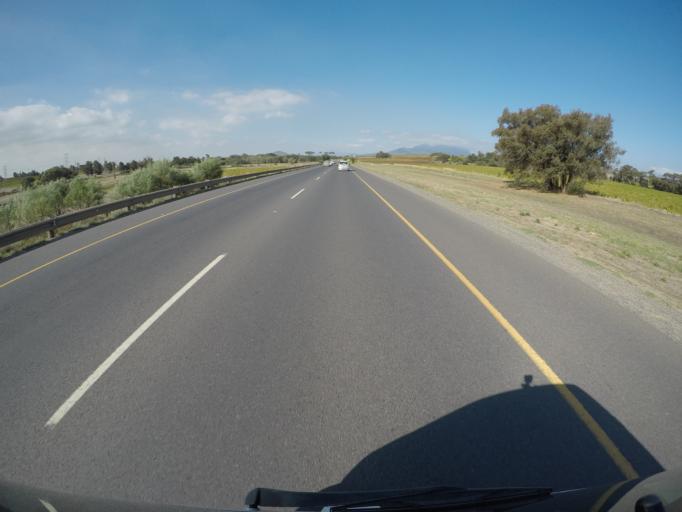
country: ZA
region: Western Cape
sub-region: City of Cape Town
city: Kraaifontein
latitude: -33.8823
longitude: 18.7571
